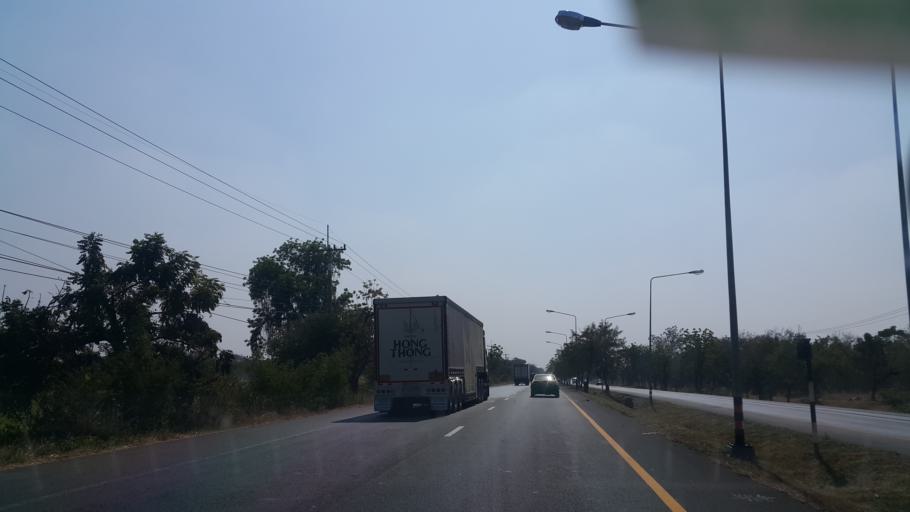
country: TH
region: Nakhon Ratchasima
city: Non Daeng
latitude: 15.3759
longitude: 102.4601
